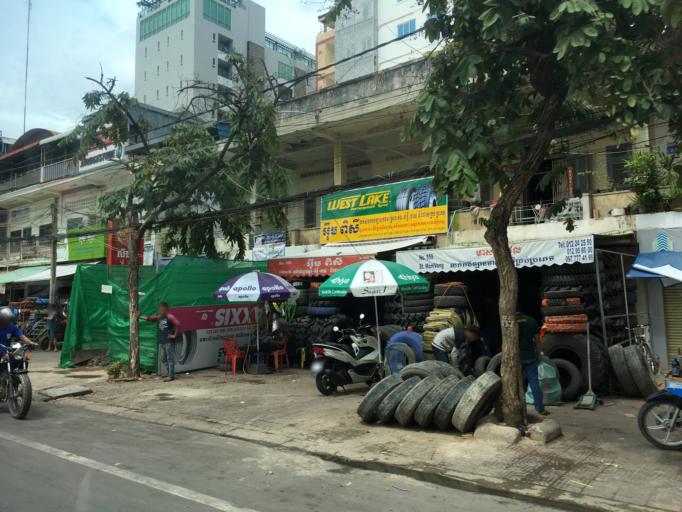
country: KH
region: Phnom Penh
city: Phnom Penh
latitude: 11.5526
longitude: 104.9210
